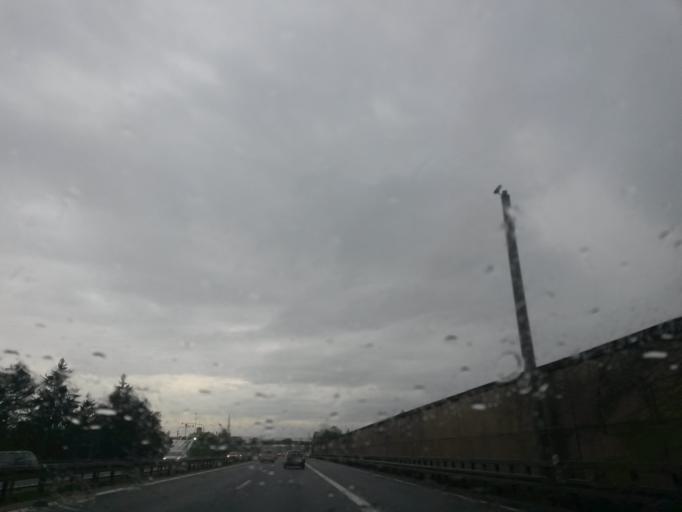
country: DE
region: Bavaria
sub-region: Regierungsbezirk Mittelfranken
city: Baiersdorf
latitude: 49.6603
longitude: 11.0383
